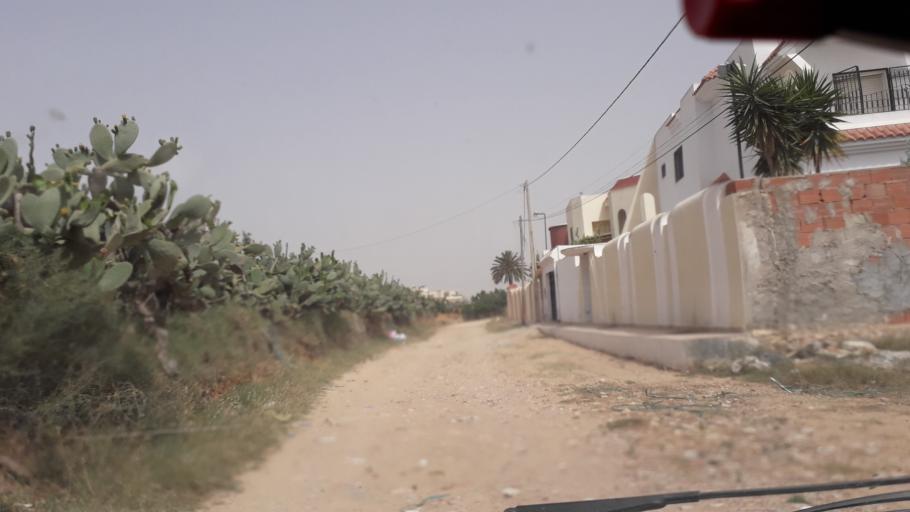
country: TN
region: Safaqis
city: Al Qarmadah
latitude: 34.8045
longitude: 10.7740
